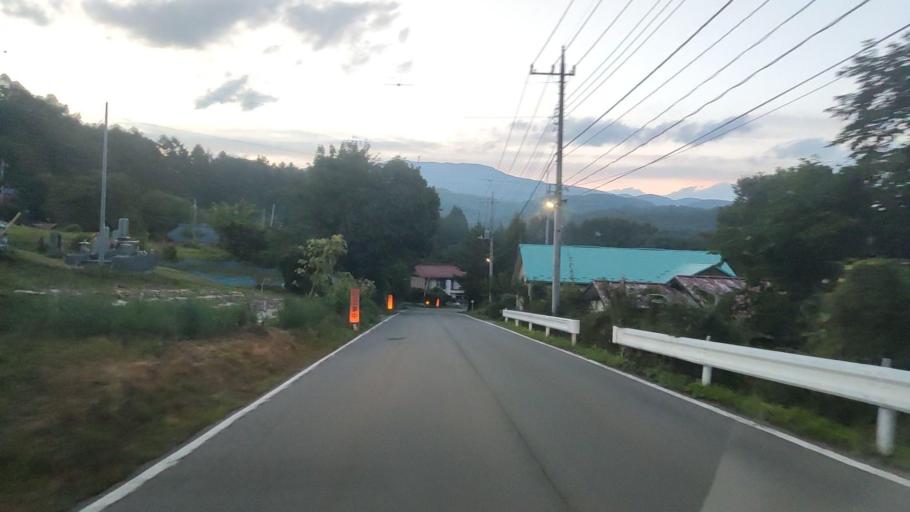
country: JP
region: Gunma
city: Nakanojomachi
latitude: 36.5423
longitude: 138.6027
